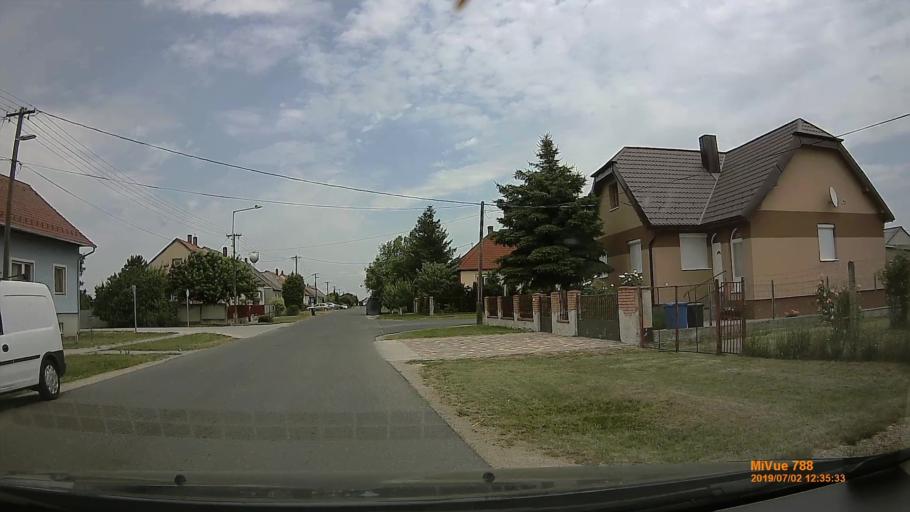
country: HU
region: Gyor-Moson-Sopron
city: Janossomorja
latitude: 47.8542
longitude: 17.1722
